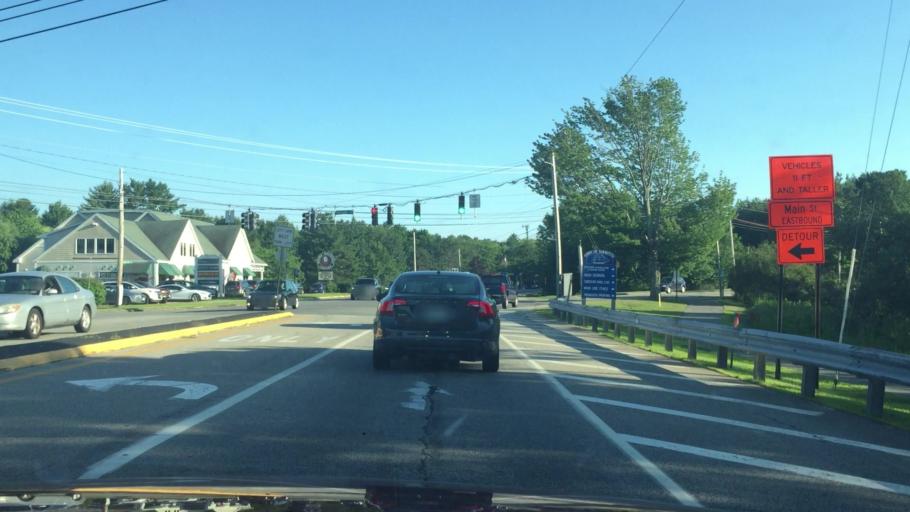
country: US
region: Maine
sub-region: Cumberland County
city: Yarmouth
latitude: 43.7931
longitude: -70.1887
